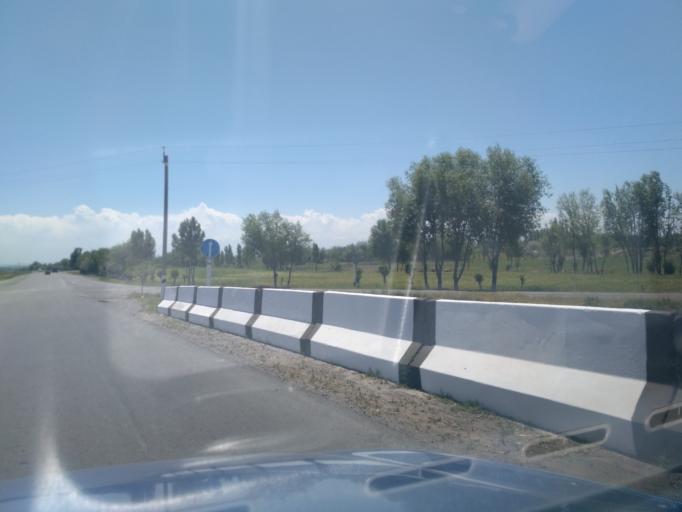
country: UZ
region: Sirdaryo
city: Yangiyer
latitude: 40.2375
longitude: 68.8449
